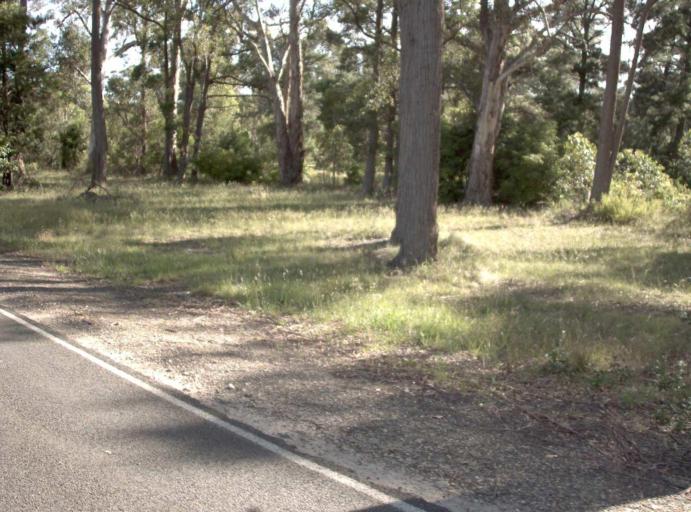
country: AU
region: Victoria
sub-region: East Gippsland
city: Lakes Entrance
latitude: -37.6910
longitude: 148.4688
